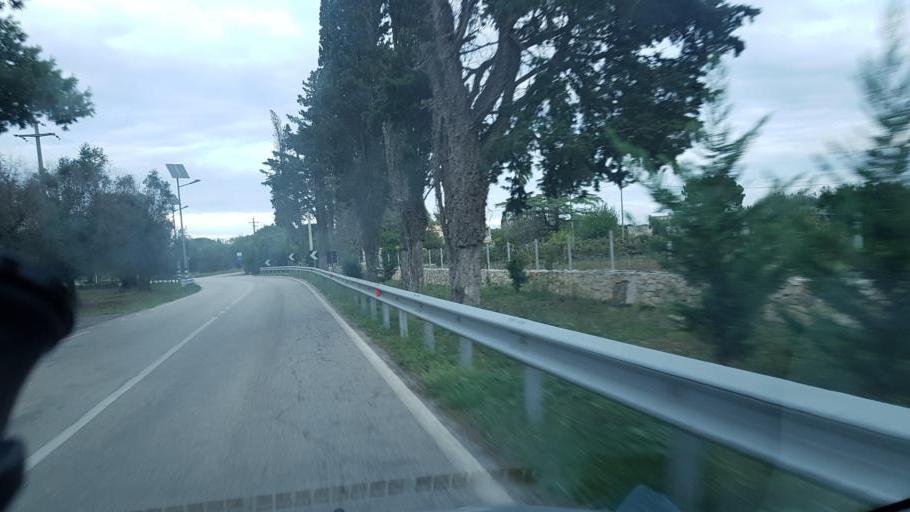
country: IT
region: Apulia
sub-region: Provincia di Brindisi
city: Oria
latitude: 40.5182
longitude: 17.6770
